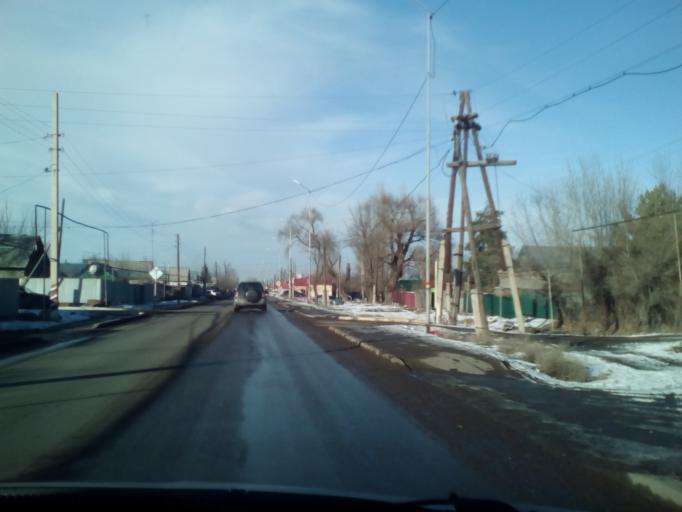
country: KZ
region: Almaty Oblysy
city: Burunday
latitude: 43.1706
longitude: 76.4160
